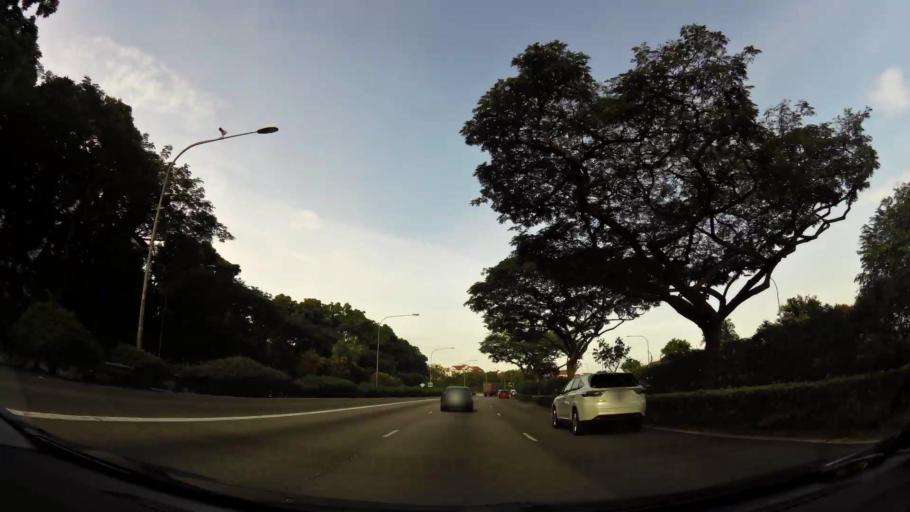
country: MY
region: Johor
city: Johor Bahru
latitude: 1.3451
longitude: 103.7390
